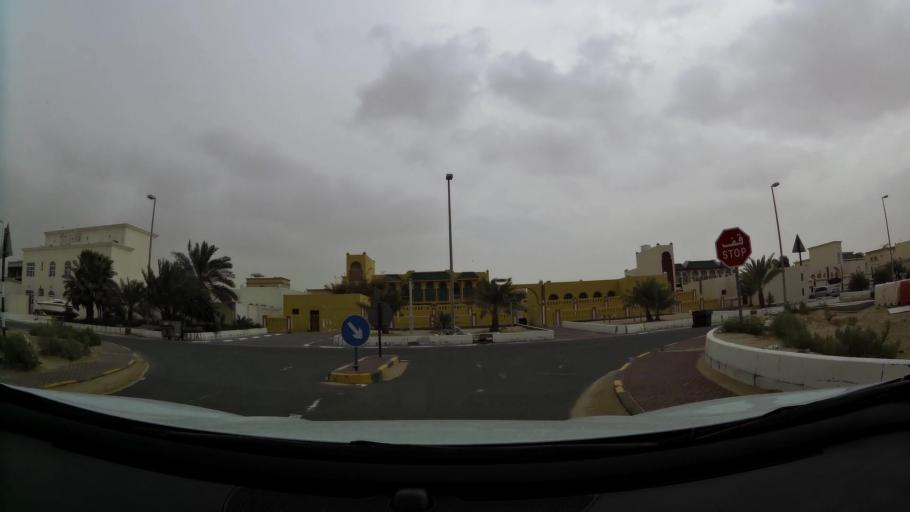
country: AE
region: Abu Dhabi
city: Abu Dhabi
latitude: 24.3751
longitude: 54.6699
